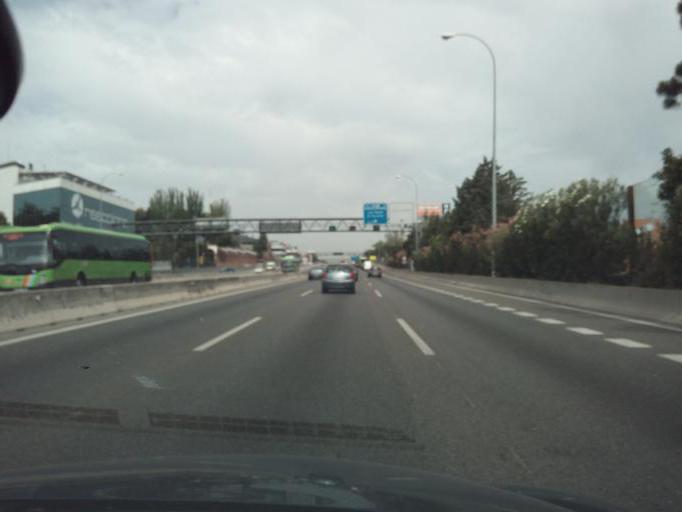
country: ES
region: Madrid
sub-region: Provincia de Madrid
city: Majadahonda
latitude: 40.4820
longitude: -3.8549
